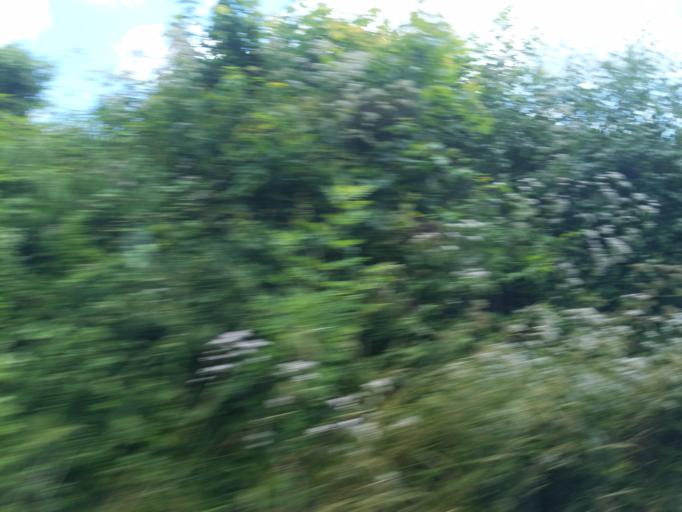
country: GB
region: England
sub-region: Cornwall
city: Par
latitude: 50.3682
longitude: -4.6840
